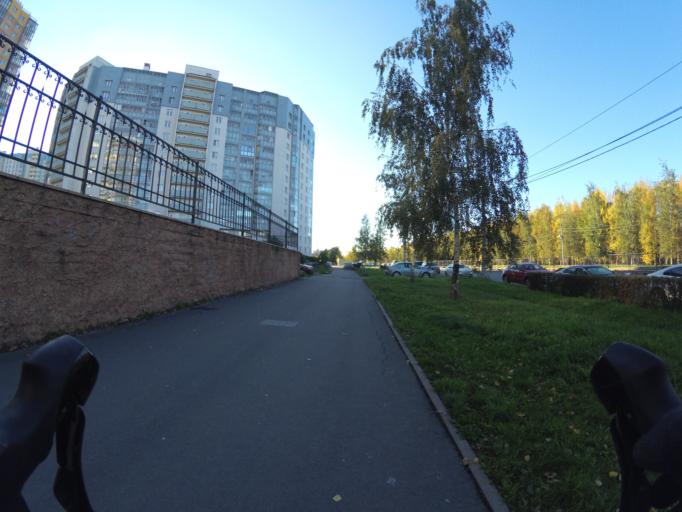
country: RU
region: Leningrad
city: Untolovo
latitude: 59.9996
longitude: 30.1939
